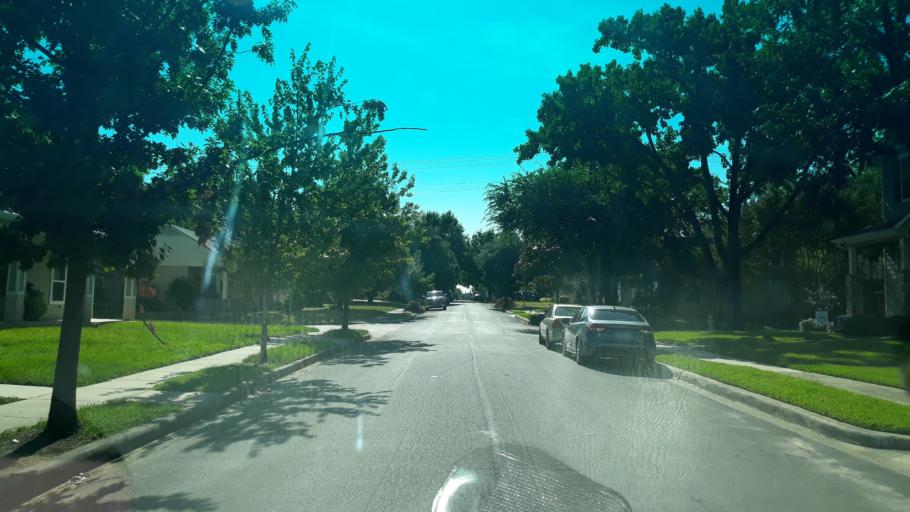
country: US
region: Texas
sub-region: Dallas County
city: Highland Park
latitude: 32.8238
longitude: -96.7633
